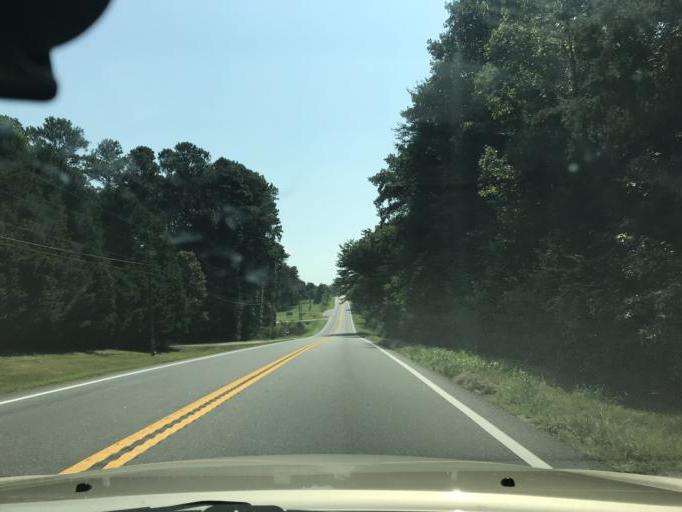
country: US
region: Georgia
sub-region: Hall County
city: Flowery Branch
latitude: 34.2510
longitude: -84.0057
